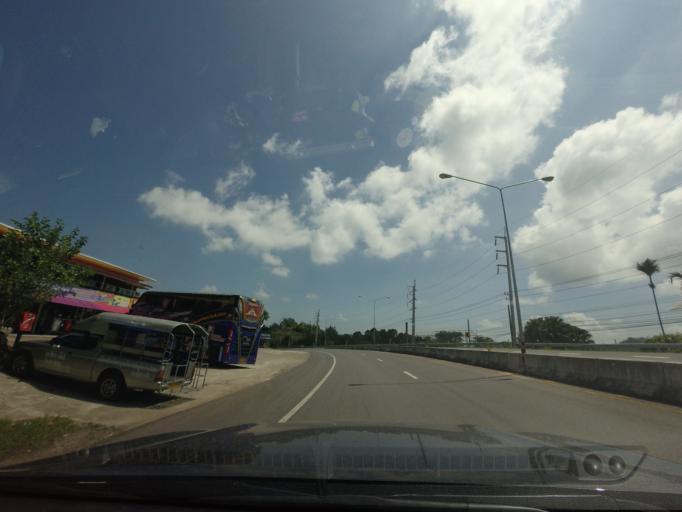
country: TH
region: Phetchabun
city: Khao Kho
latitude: 16.7689
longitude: 101.0530
